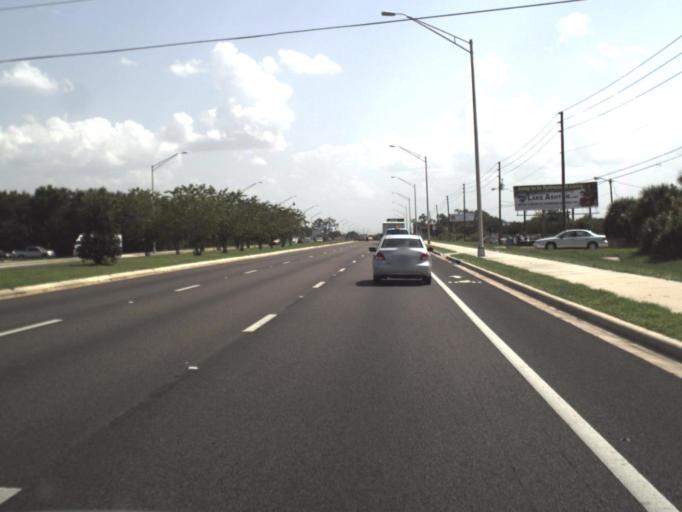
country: US
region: Florida
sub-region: Polk County
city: Lake Hamilton
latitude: 28.0294
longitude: -81.6351
